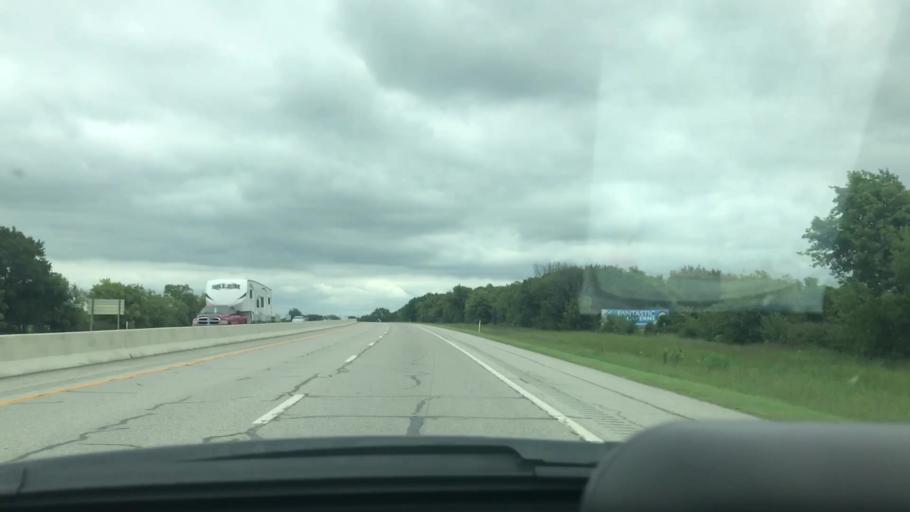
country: US
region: Oklahoma
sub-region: Ottawa County
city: Afton
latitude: 36.7348
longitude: -94.9123
